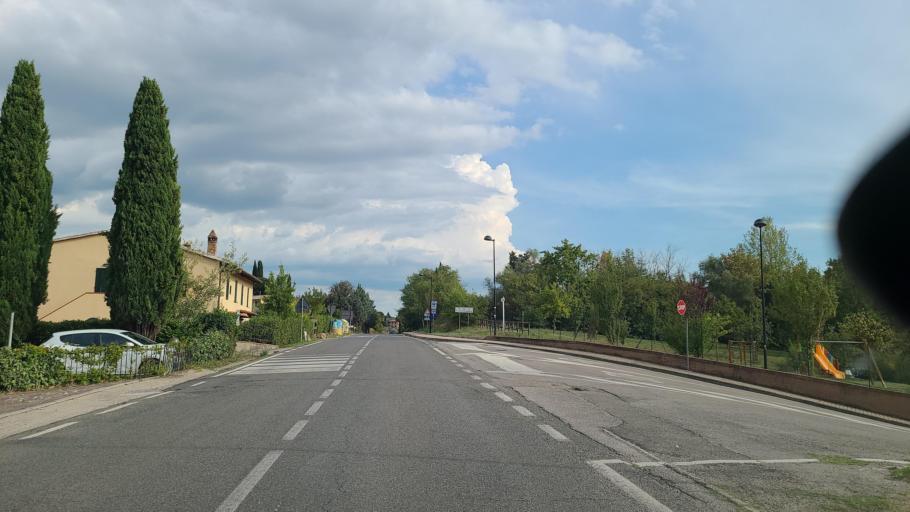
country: IT
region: Tuscany
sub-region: Provincia di Siena
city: San Gimignano
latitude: 43.4761
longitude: 11.0296
